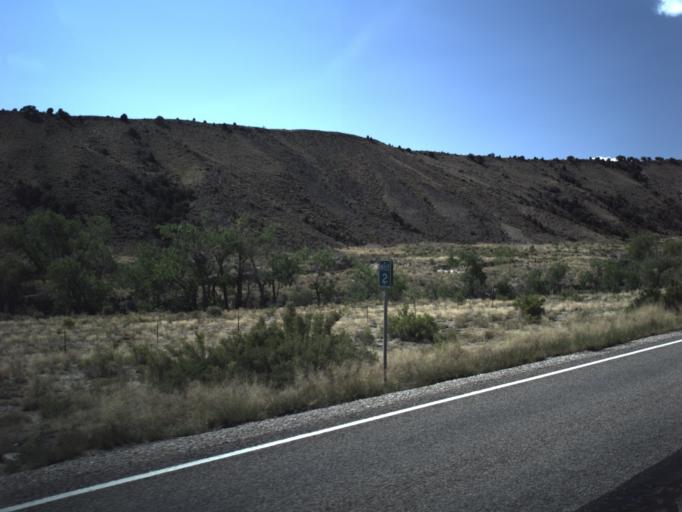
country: US
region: Utah
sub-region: Emery County
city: Ferron
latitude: 38.7930
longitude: -111.3468
